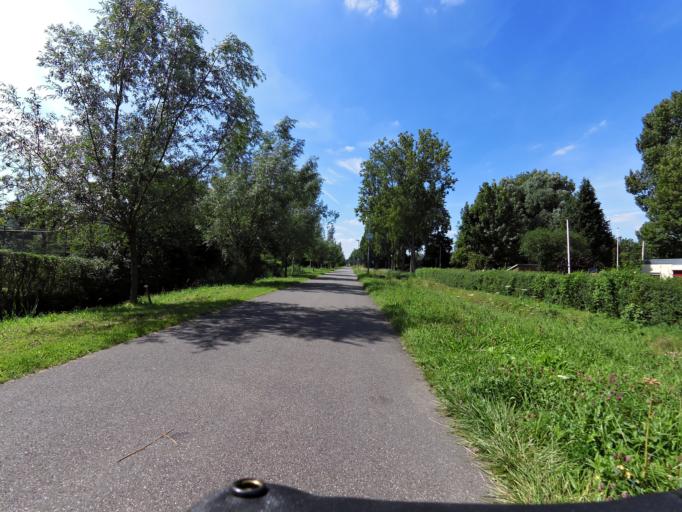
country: NL
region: South Holland
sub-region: Gemeente Binnenmaas
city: Heinenoord
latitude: 51.8691
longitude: 4.4831
